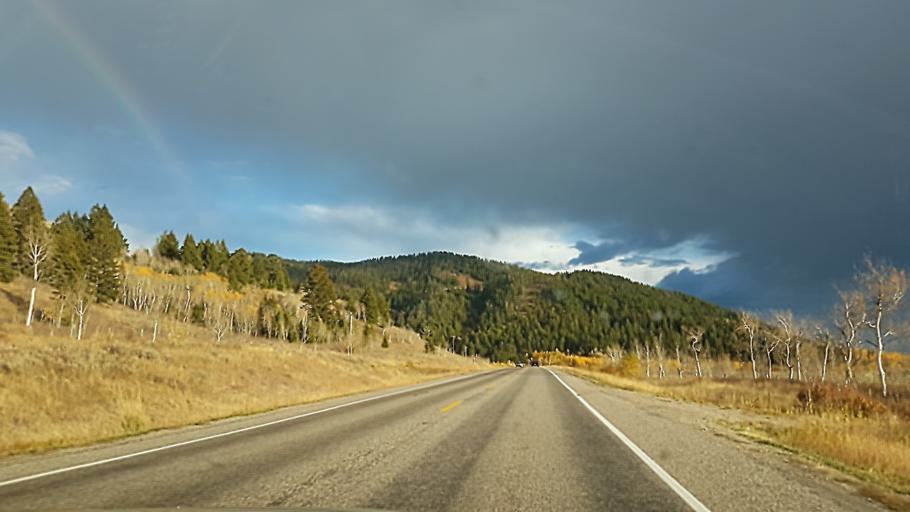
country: US
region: Montana
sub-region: Gallatin County
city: West Yellowstone
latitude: 44.6404
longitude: -111.3350
